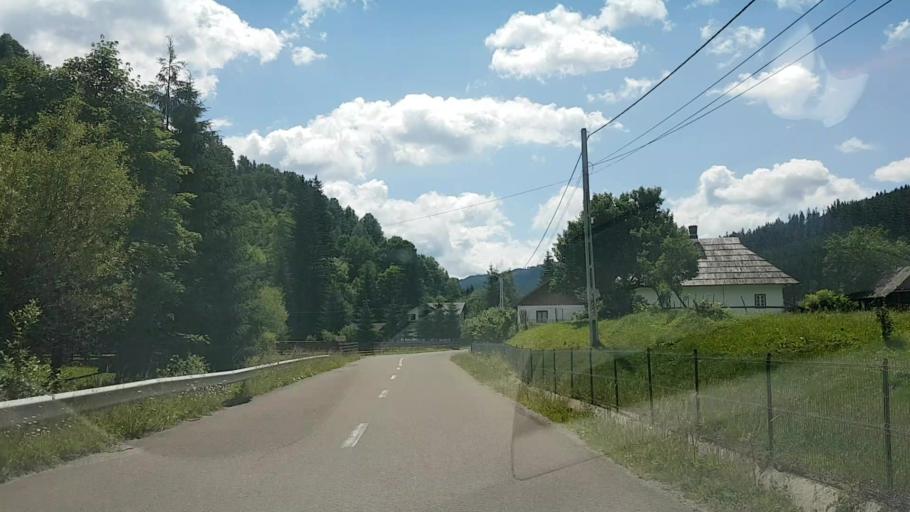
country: RO
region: Suceava
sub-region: Comuna Pojorata
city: Pojorata
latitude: 47.4946
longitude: 25.4830
